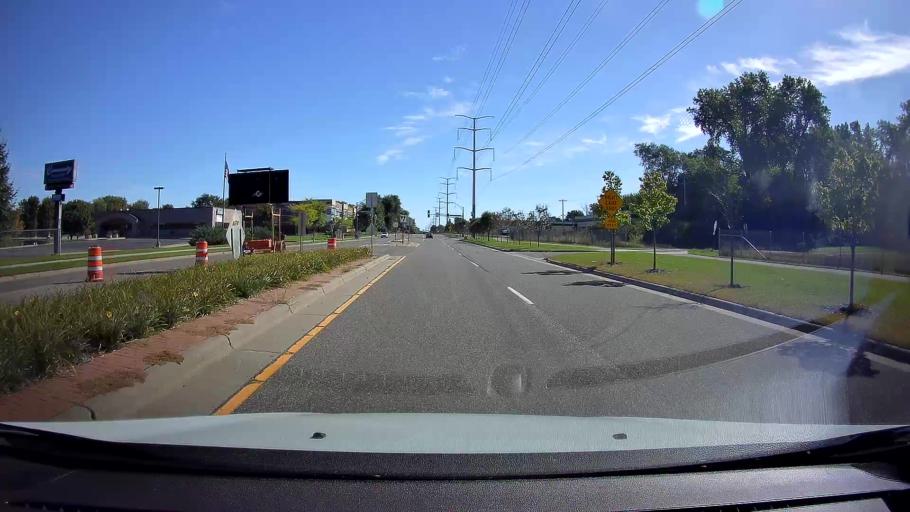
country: US
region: Minnesota
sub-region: Ramsey County
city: Roseville
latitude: 45.0209
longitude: -93.1648
